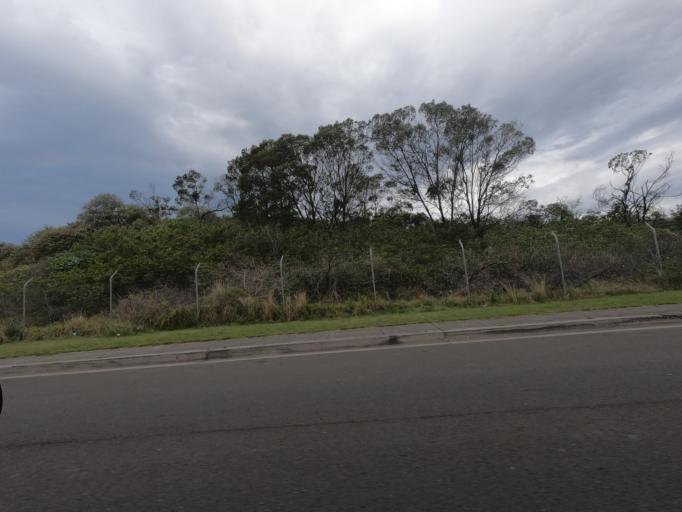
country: AU
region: New South Wales
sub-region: Wollongong
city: Cordeaux Heights
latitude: -34.4610
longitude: 150.8441
